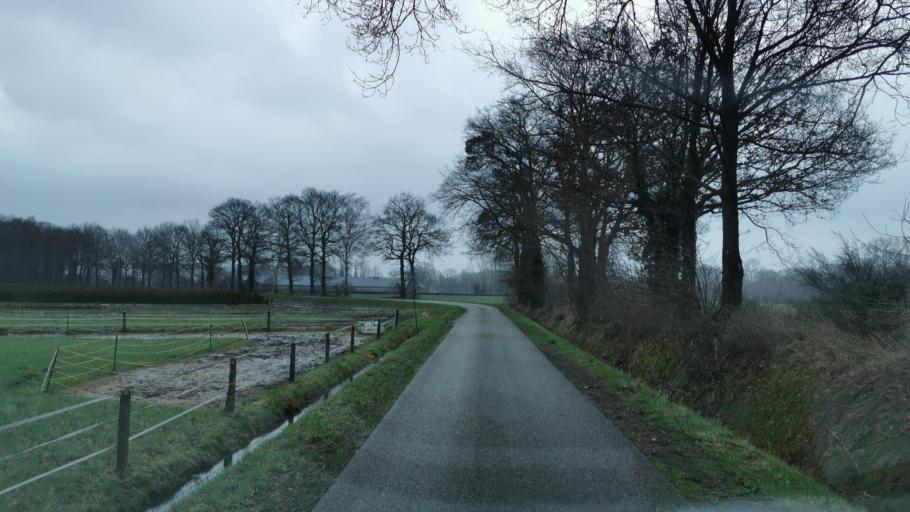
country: NL
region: Overijssel
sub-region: Gemeente Hengelo
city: Hengelo
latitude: 52.3277
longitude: 6.8285
